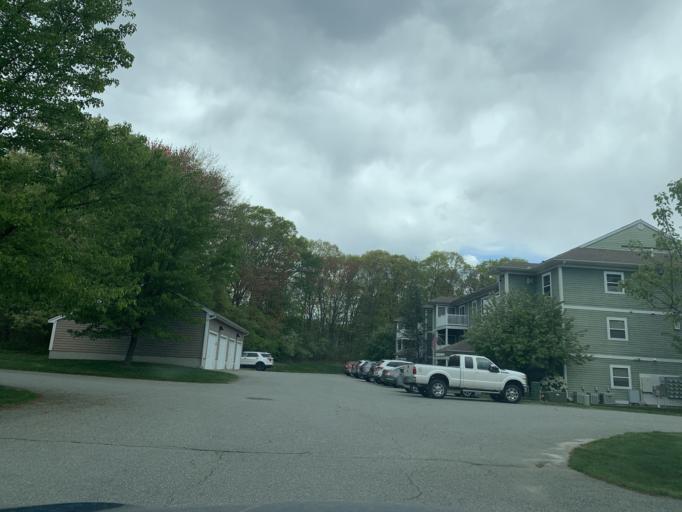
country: US
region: Rhode Island
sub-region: Kent County
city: East Greenwich
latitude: 41.6726
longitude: -71.4915
